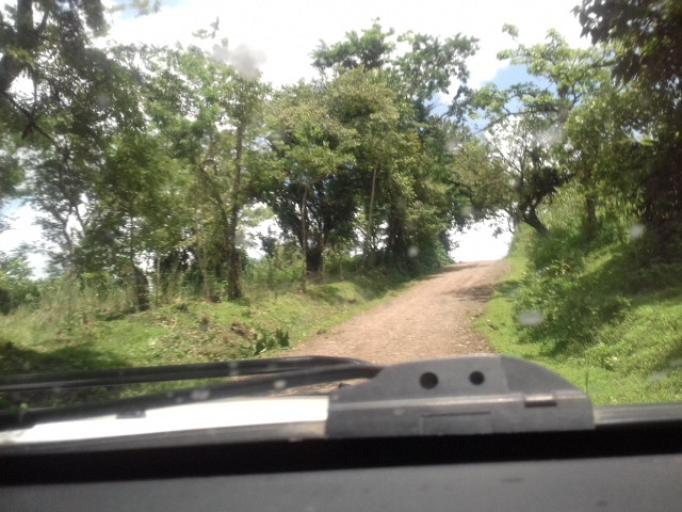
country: NI
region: Matagalpa
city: Rio Blanco
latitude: 12.9818
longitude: -85.3735
